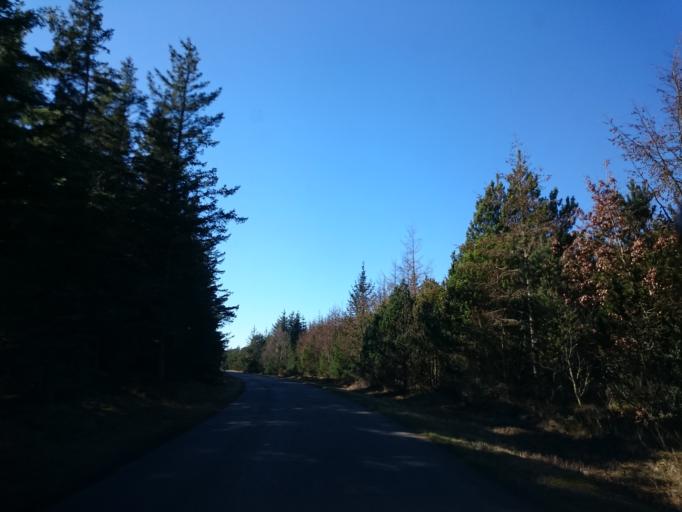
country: DK
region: North Denmark
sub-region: Hjorring Kommune
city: Sindal
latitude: 57.6258
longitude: 10.3279
